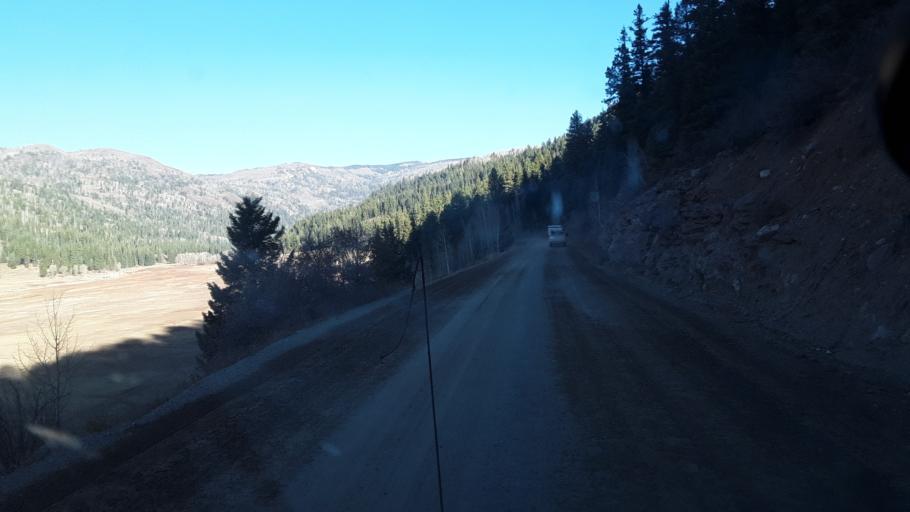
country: US
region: Colorado
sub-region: La Plata County
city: Bayfield
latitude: 37.4158
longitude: -107.6643
